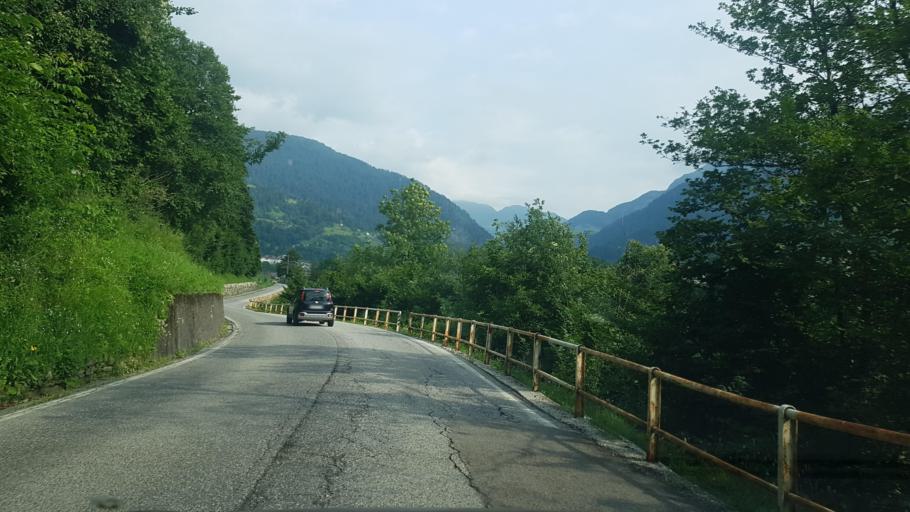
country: IT
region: Friuli Venezia Giulia
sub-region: Provincia di Udine
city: Paularo
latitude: 46.5234
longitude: 13.1220
